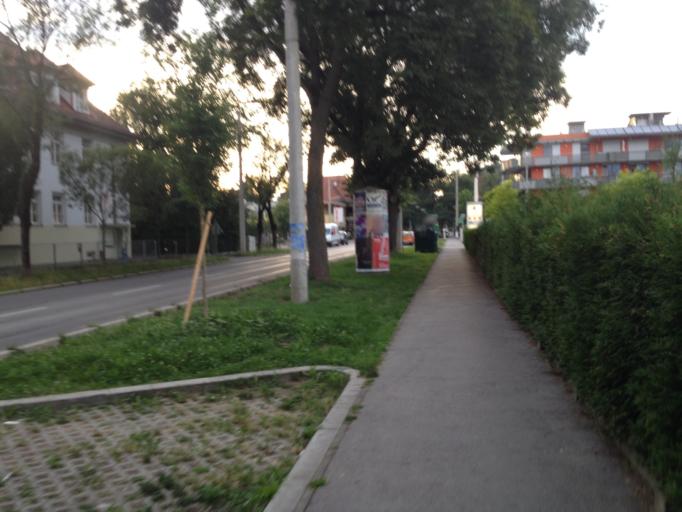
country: AT
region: Styria
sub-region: Graz Stadt
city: Graz
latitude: 47.0879
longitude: 15.4293
